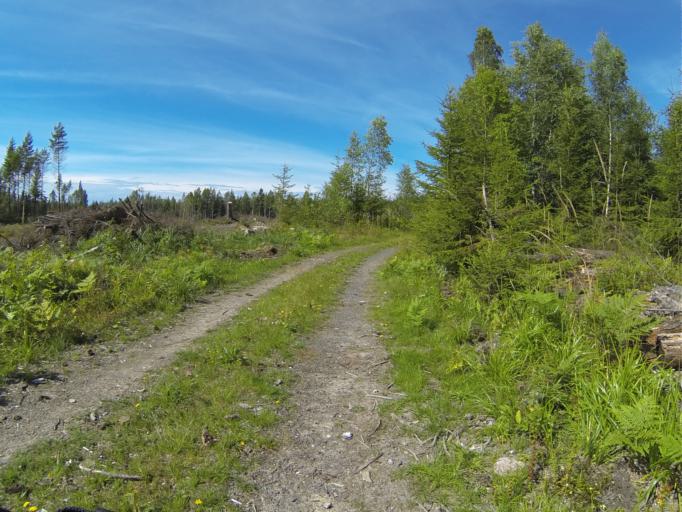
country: FI
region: Varsinais-Suomi
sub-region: Salo
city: Pernioe
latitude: 60.2802
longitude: 23.0546
